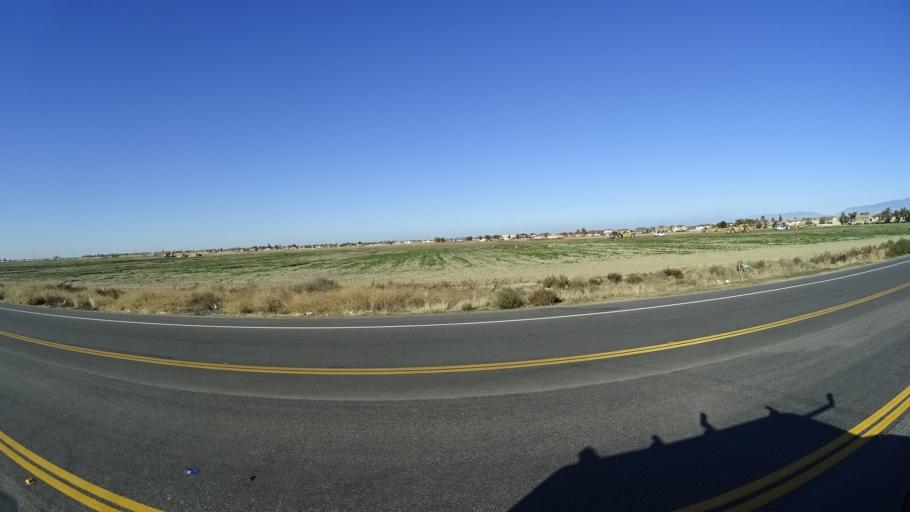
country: US
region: California
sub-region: Kern County
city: Greenfield
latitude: 35.2815
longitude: -119.0683
